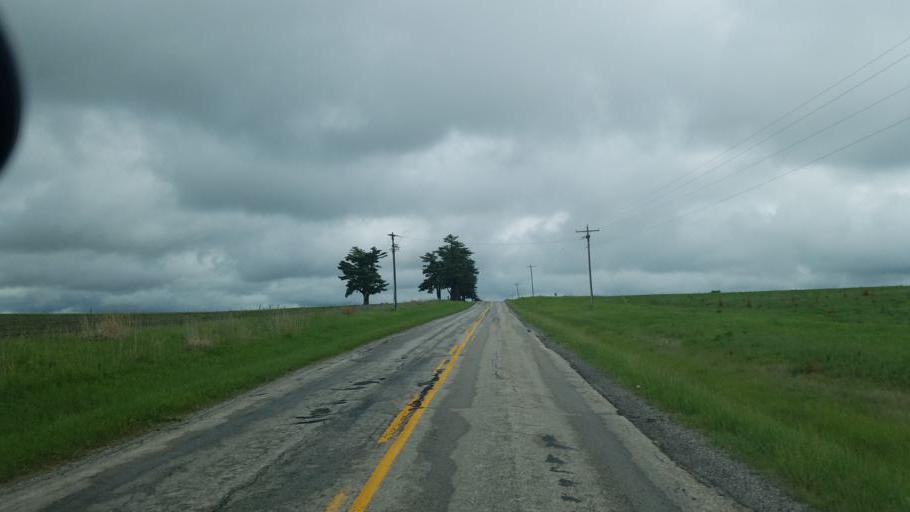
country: US
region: Missouri
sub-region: Mercer County
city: Princeton
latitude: 40.4319
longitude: -93.6847
